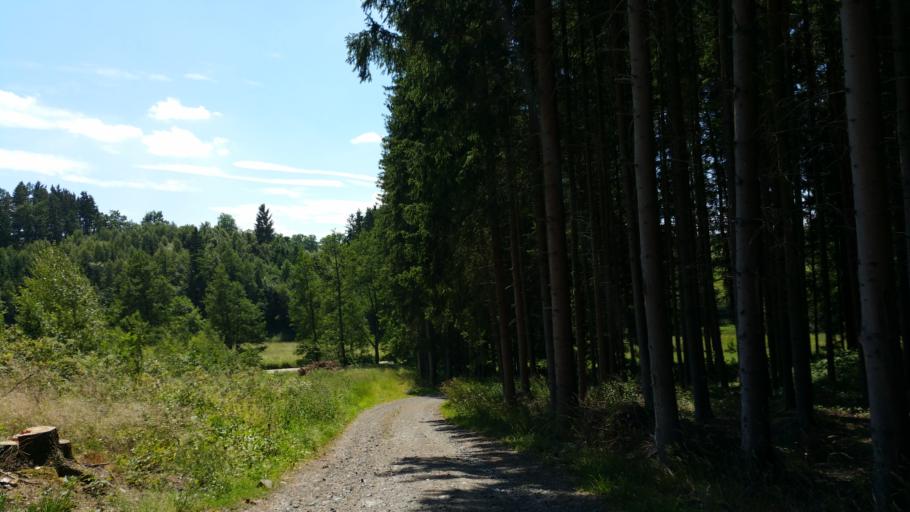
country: DE
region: Bavaria
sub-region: Upper Franconia
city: Koditz
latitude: 50.3485
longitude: 11.8794
